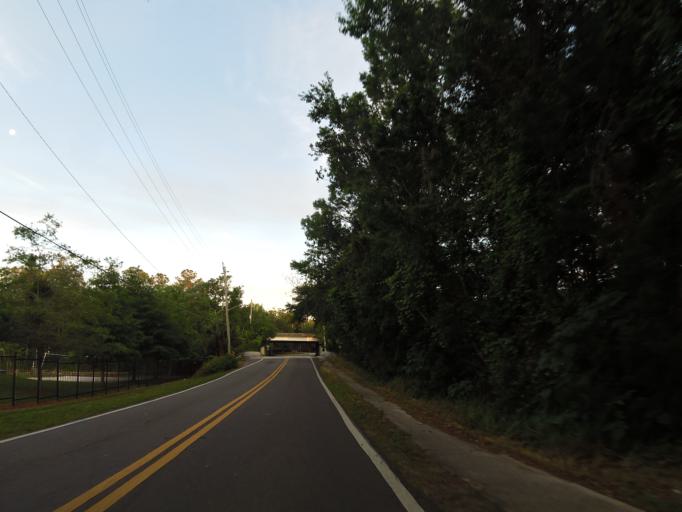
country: US
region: Florida
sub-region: Duval County
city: Jacksonville
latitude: 30.3011
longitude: -81.6140
